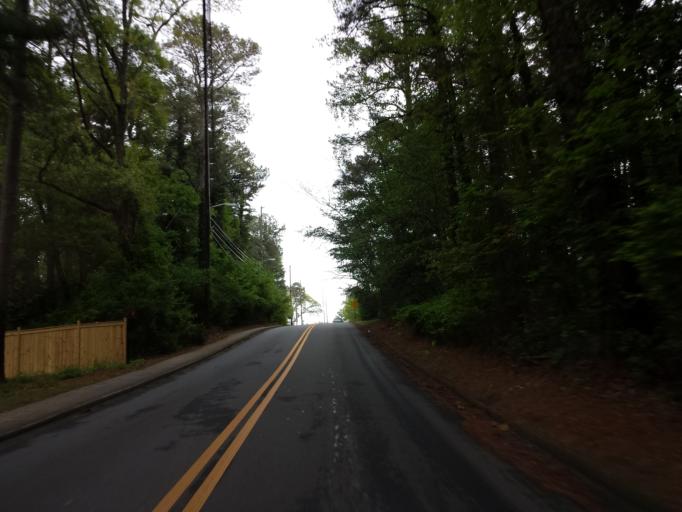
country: US
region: Georgia
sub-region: Cobb County
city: Marietta
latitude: 33.9345
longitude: -84.5619
